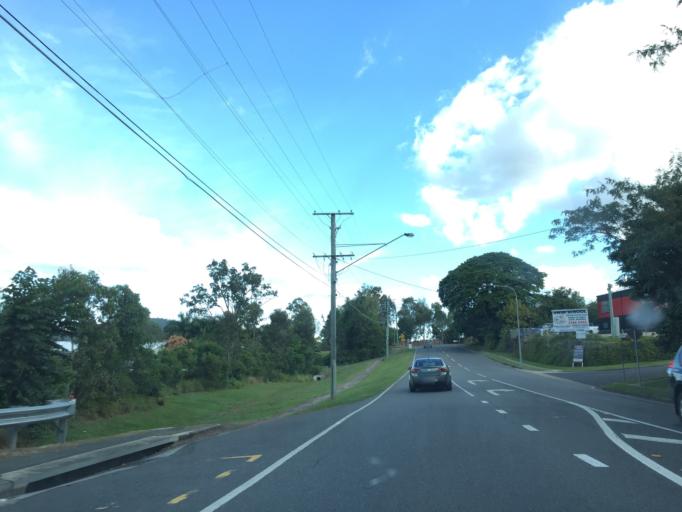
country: AU
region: Queensland
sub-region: Moreton Bay
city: Ferny Hills
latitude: -27.4313
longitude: 152.9432
